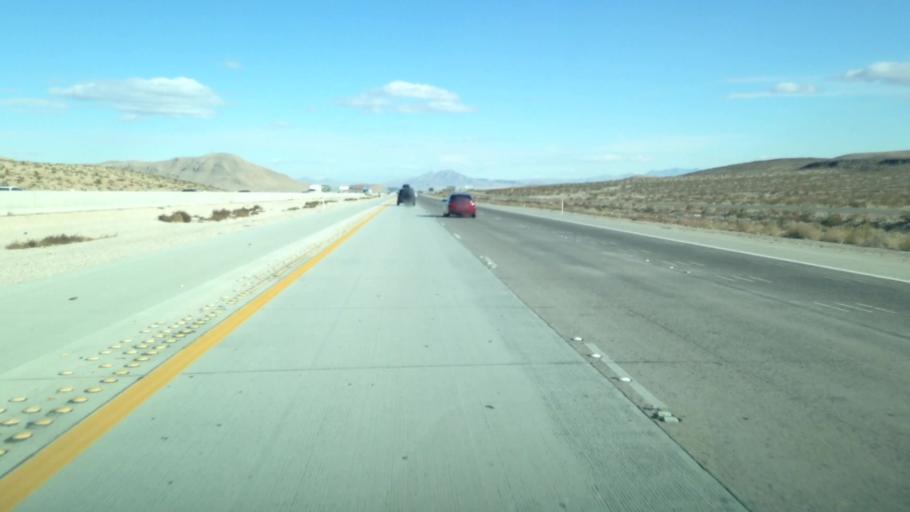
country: US
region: Nevada
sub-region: Clark County
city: Enterprise
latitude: 35.9038
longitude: -115.2118
